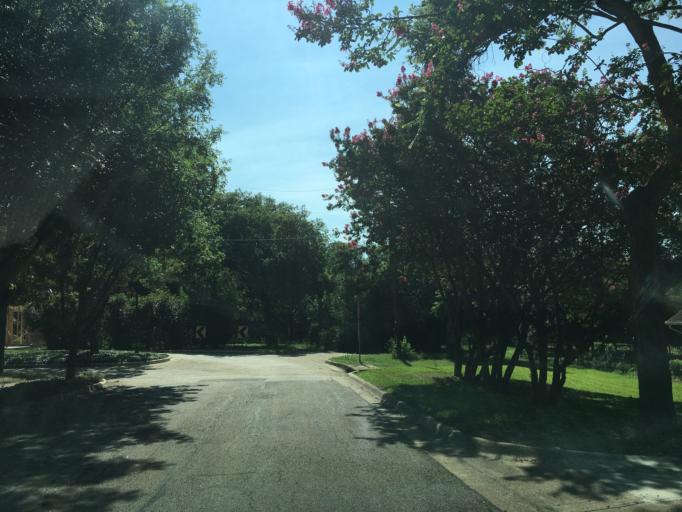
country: US
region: Texas
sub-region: Dallas County
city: Farmers Branch
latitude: 32.9184
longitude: -96.8772
